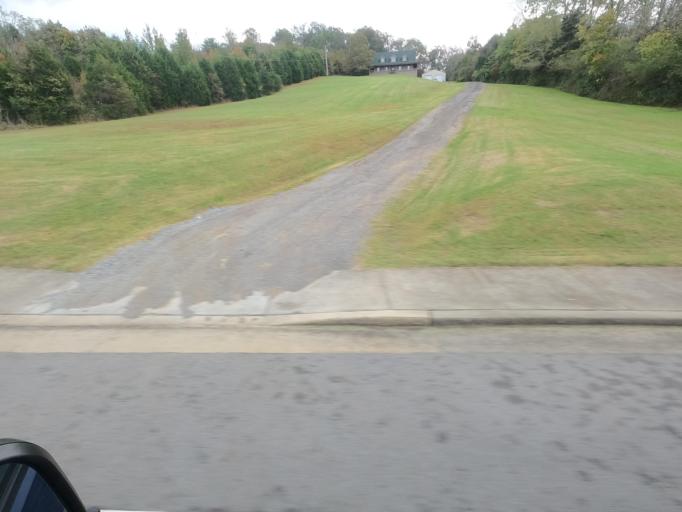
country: US
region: Tennessee
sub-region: Cheatham County
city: Kingston Springs
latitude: 36.0948
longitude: -87.0927
